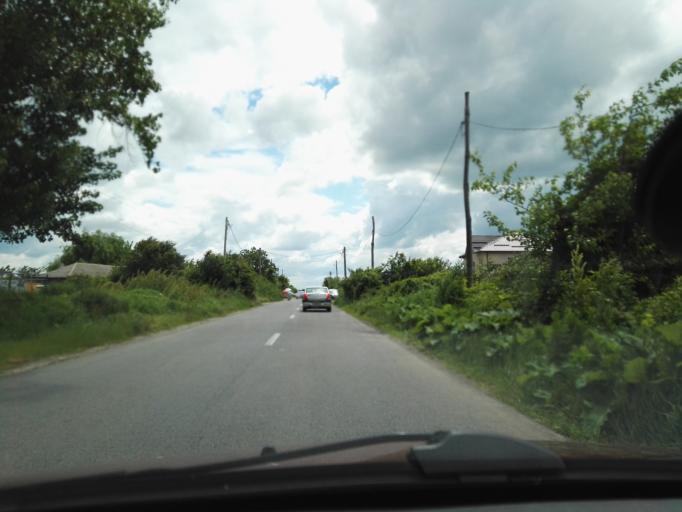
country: RO
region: Giurgiu
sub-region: Comuna Comana
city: Gradistea
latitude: 44.2261
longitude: 26.1415
